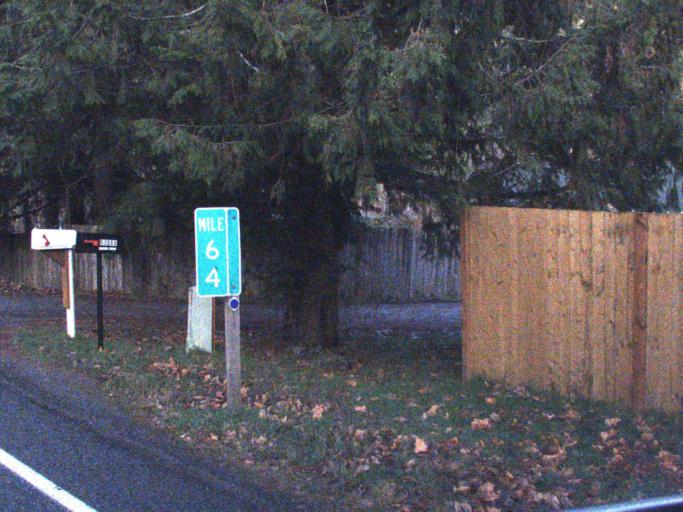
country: US
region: Washington
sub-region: Snohomish County
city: Darrington
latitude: 48.4420
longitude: -121.5795
